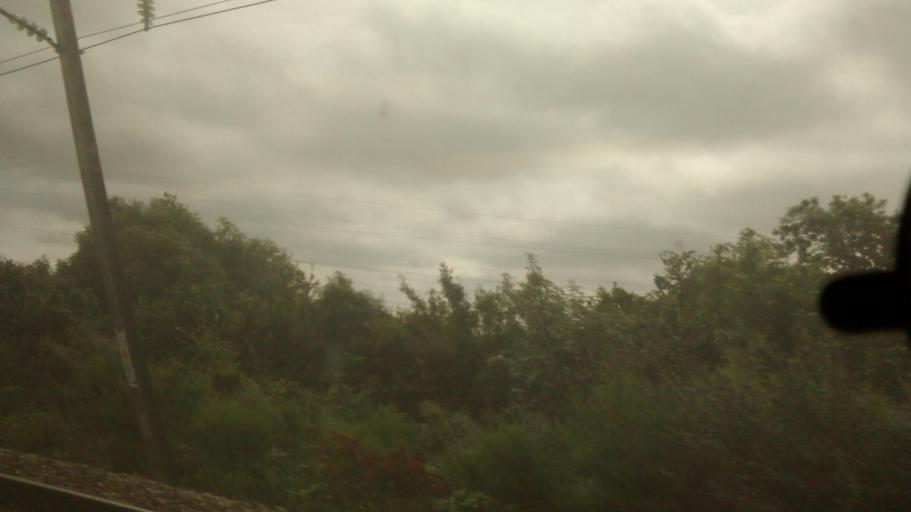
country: FR
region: Ile-de-France
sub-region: Departement de l'Essonne
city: Vaugrigneuse
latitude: 48.6130
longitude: 2.1188
